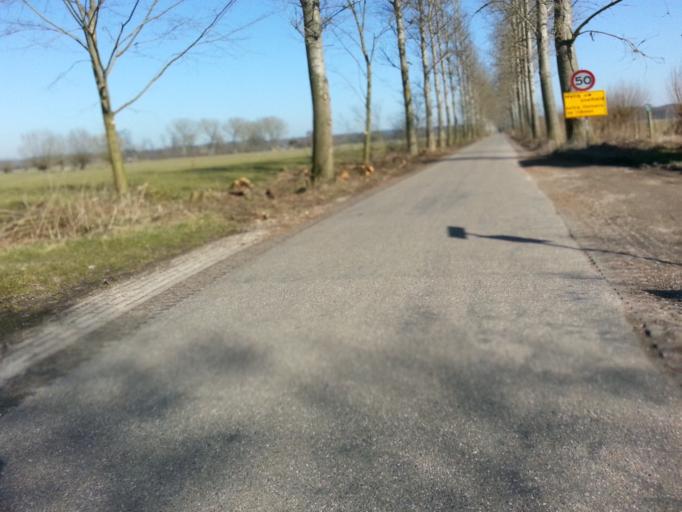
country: NL
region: Utrecht
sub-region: Gemeente Utrechtse Heuvelrug
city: Doorn
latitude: 52.0025
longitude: 5.3808
